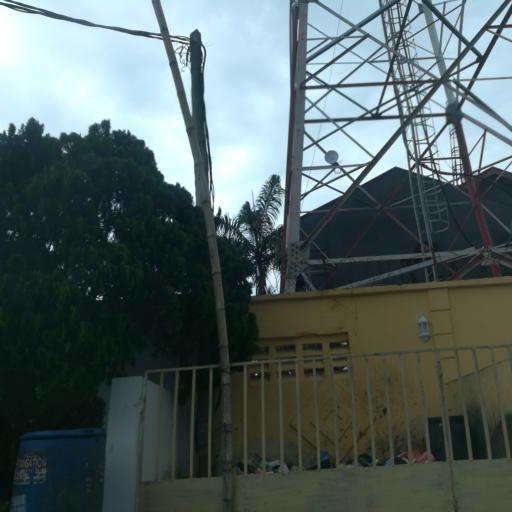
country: NG
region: Lagos
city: Ikoyi
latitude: 6.4381
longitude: 3.4626
